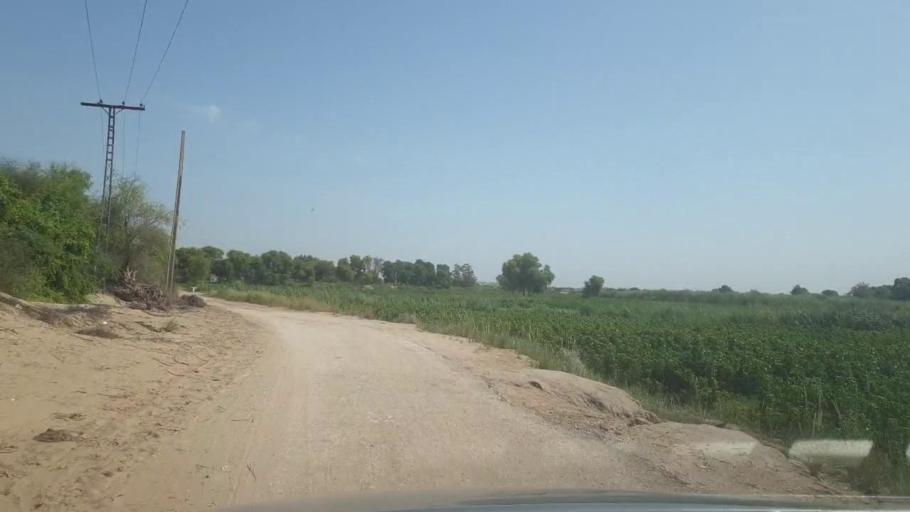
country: PK
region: Sindh
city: Khairpur
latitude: 27.4030
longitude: 69.0812
